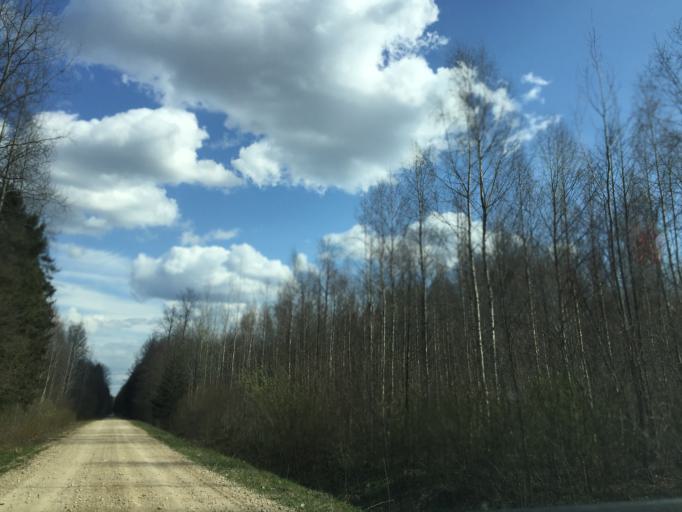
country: LV
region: Skriveri
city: Skriveri
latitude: 56.7999
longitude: 25.2039
